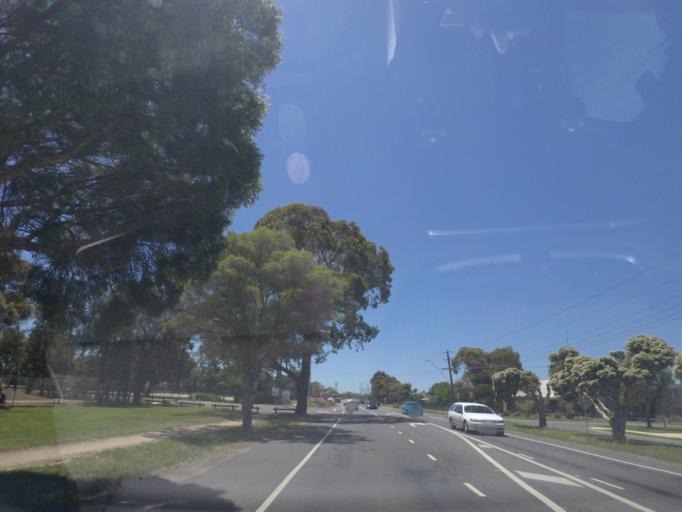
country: AU
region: Victoria
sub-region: Whittlesea
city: Epping
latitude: -37.6410
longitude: 145.0265
